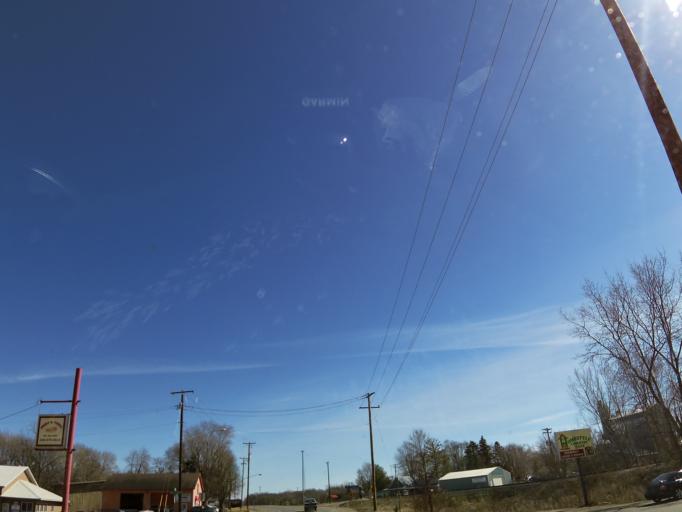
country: US
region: Minnesota
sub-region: Wright County
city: Annandale
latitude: 45.2608
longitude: -94.1225
